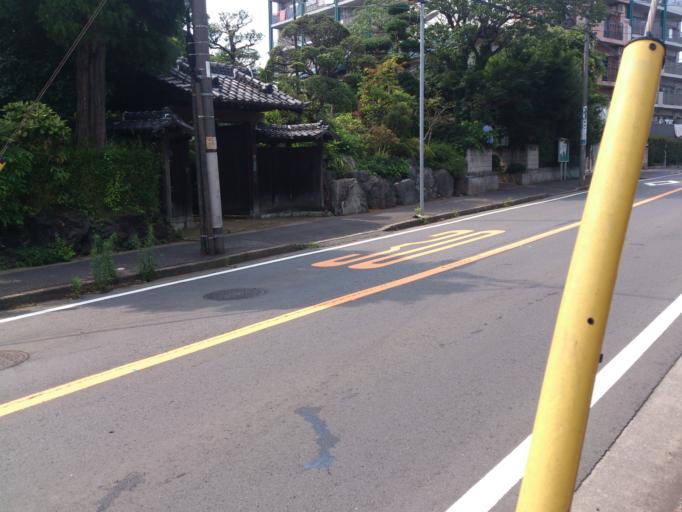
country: JP
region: Chiba
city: Nagareyama
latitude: 35.8235
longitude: 139.9333
